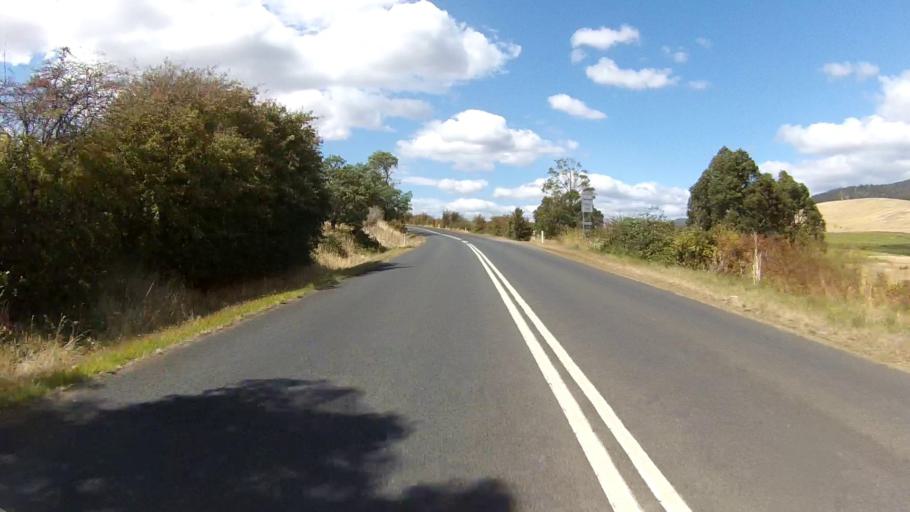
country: AU
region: Tasmania
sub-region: Derwent Valley
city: New Norfolk
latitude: -42.7363
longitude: 146.9292
